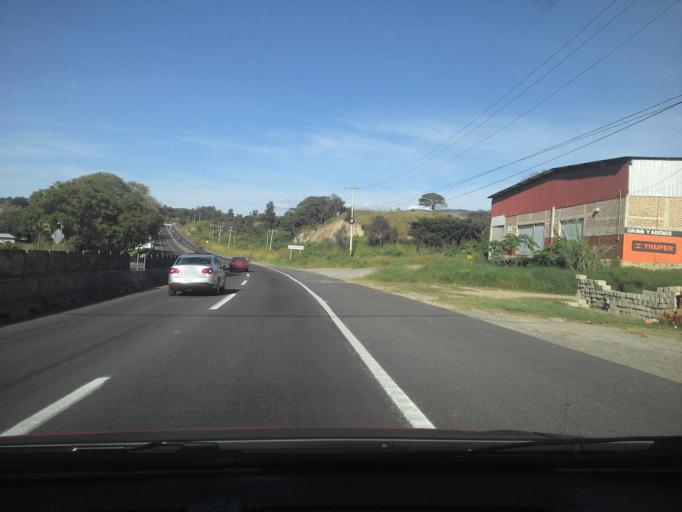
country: MX
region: Jalisco
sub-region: Tala
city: Los Ruisenores
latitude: 20.7215
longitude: -103.6235
